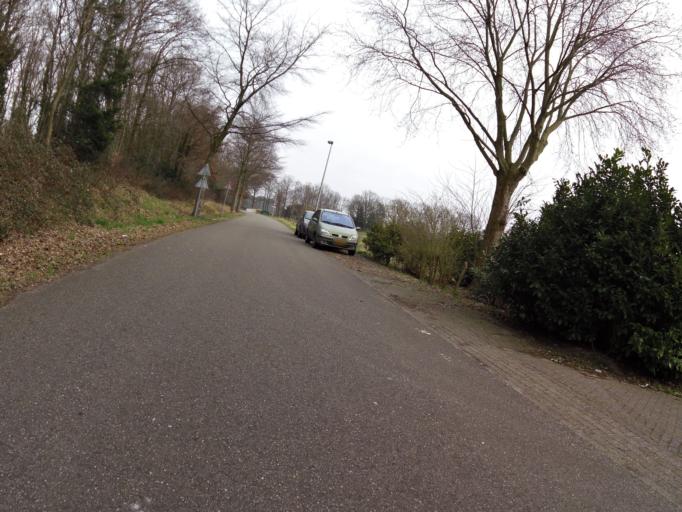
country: NL
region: North Brabant
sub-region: Gemeente Heusden
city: Heusden
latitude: 51.6769
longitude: 5.1426
